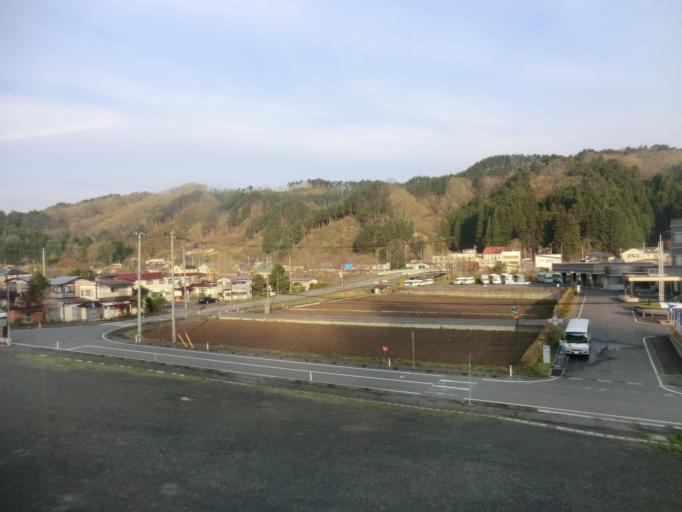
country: JP
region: Iwate
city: Miyako
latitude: 40.0048
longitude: 141.8868
